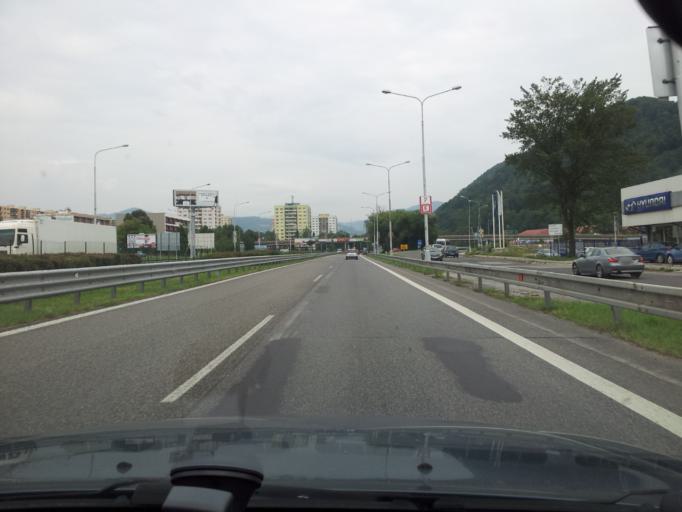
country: SK
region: Banskobystricky
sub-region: Okres Banska Bystrica
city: Banska Bystrica
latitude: 48.7140
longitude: 19.1382
